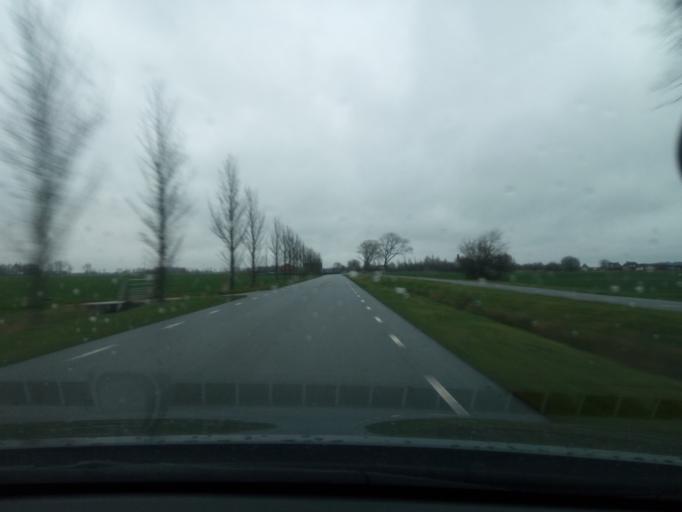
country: NL
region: Groningen
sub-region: Gemeente Winsum
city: Winsum
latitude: 53.3375
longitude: 6.5575
